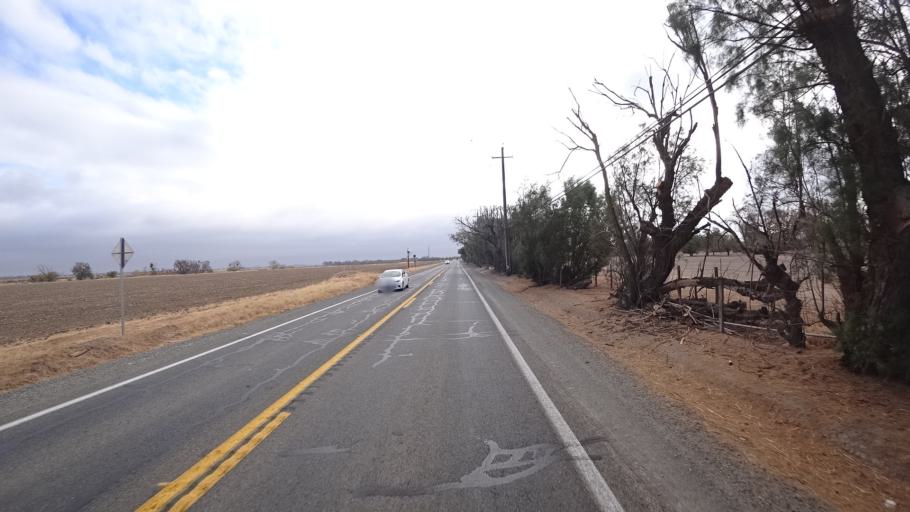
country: US
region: California
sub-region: Yolo County
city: Esparto
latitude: 38.7066
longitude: -122.0448
